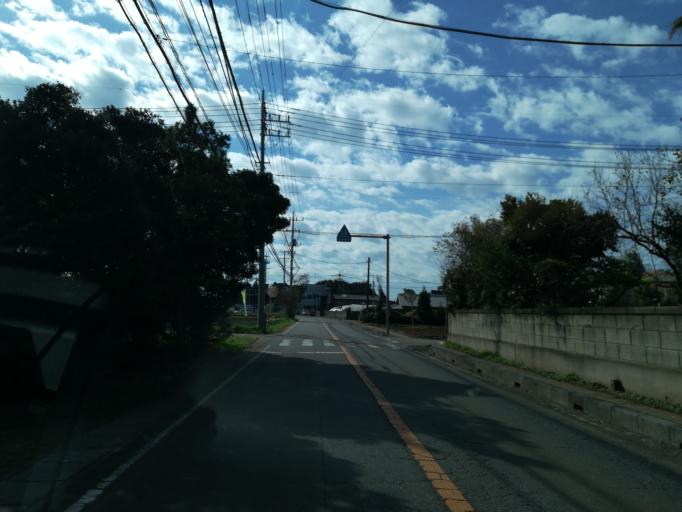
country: JP
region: Ibaraki
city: Naka
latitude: 36.0629
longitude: 140.0877
